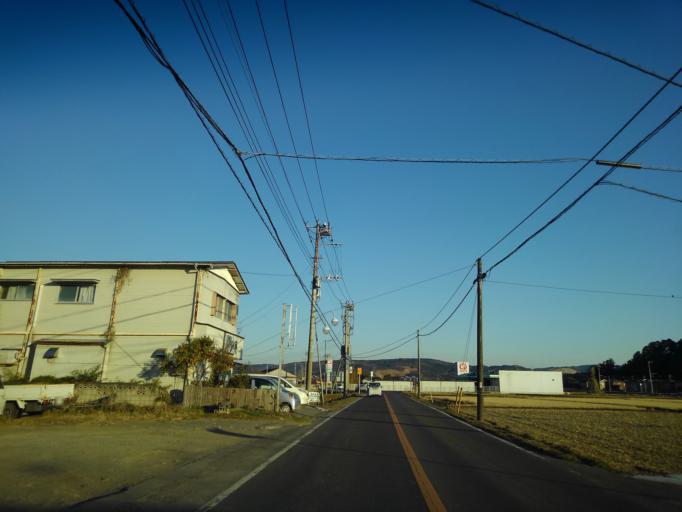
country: JP
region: Chiba
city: Kimitsu
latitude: 35.3050
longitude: 139.9626
